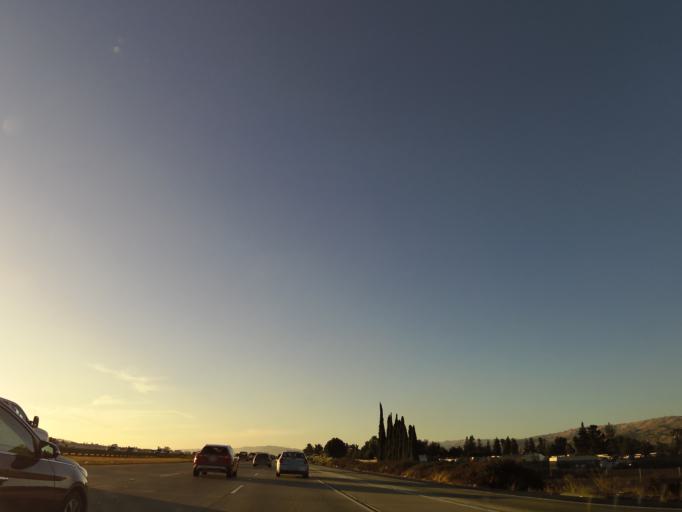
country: US
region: California
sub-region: Santa Clara County
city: San Martin
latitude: 37.0774
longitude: -121.5929
